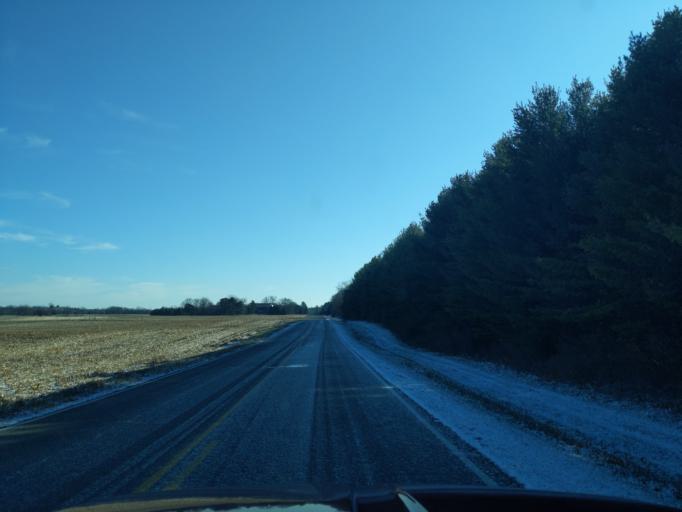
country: US
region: Wisconsin
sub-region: Waushara County
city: Silver Lake
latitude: 44.0907
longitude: -89.1763
